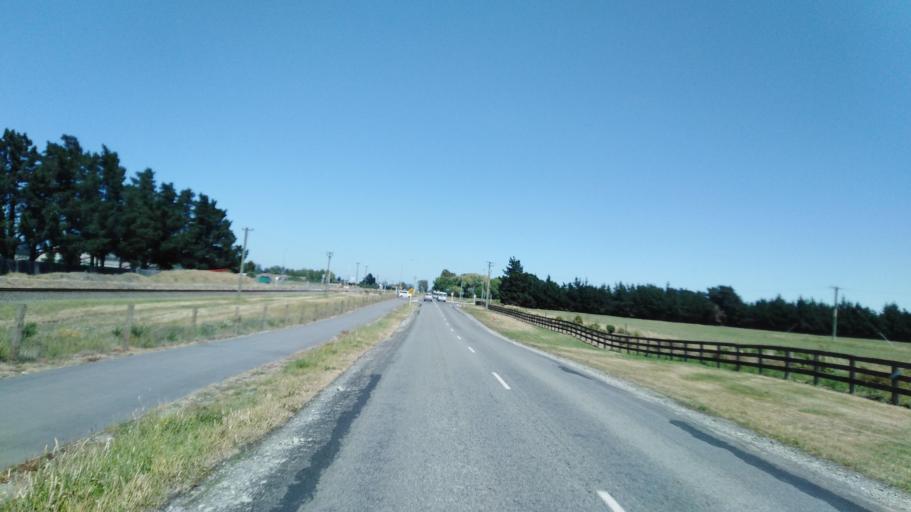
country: NZ
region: Canterbury
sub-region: Selwyn District
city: Rolleston
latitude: -43.5650
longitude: 172.4452
